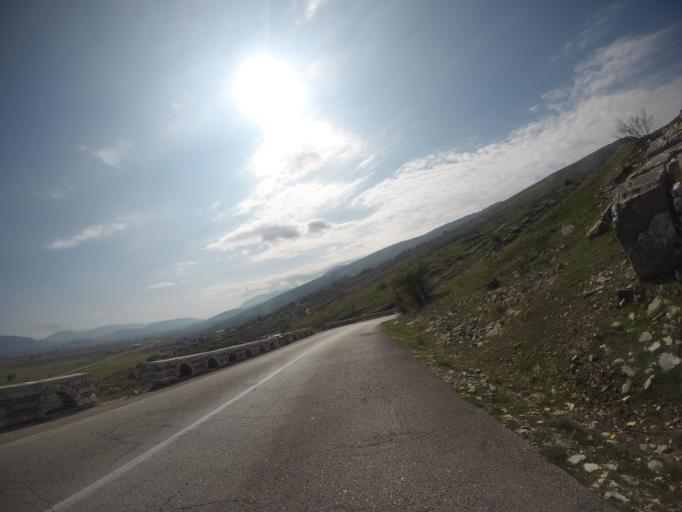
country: AL
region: Gjirokaster
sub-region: Rrethi i Gjirokastres
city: Libohove
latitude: 39.9424
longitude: 20.2605
